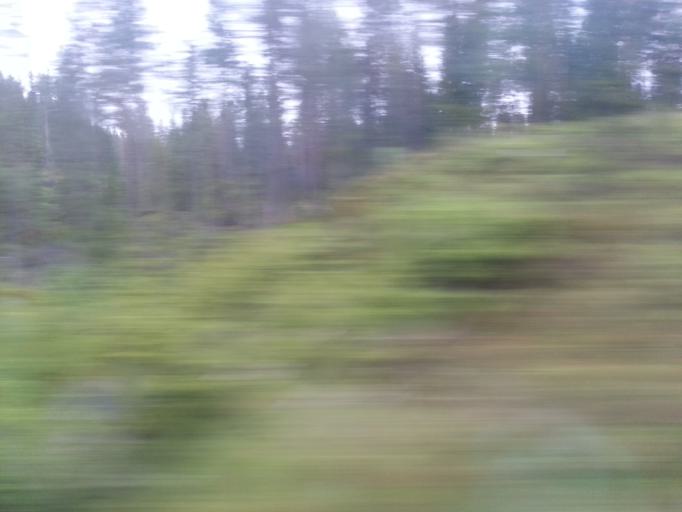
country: NO
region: Sor-Trondelag
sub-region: Rennebu
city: Berkak
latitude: 62.7226
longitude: 9.9820
